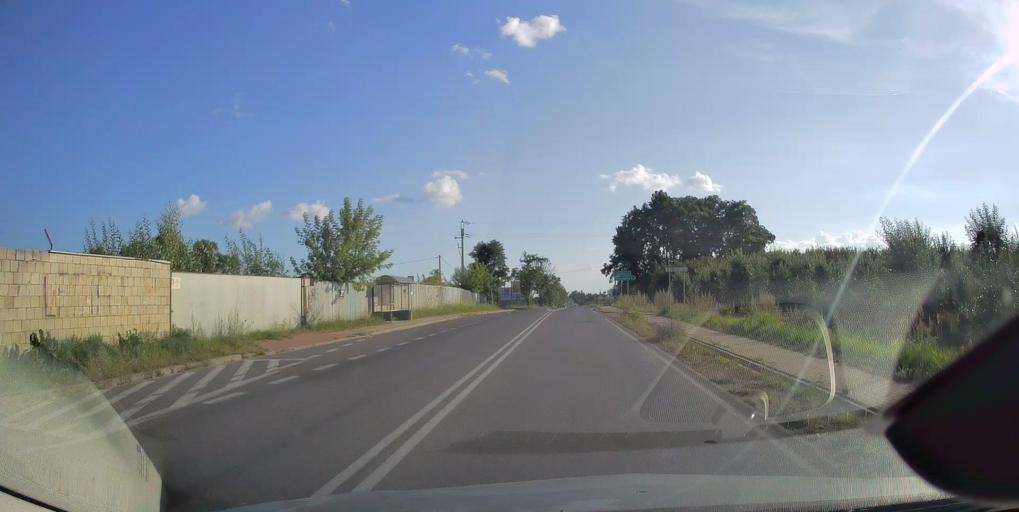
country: PL
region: Masovian Voivodeship
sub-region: Powiat grojecki
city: Belsk Duzy
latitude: 51.8370
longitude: 20.8237
